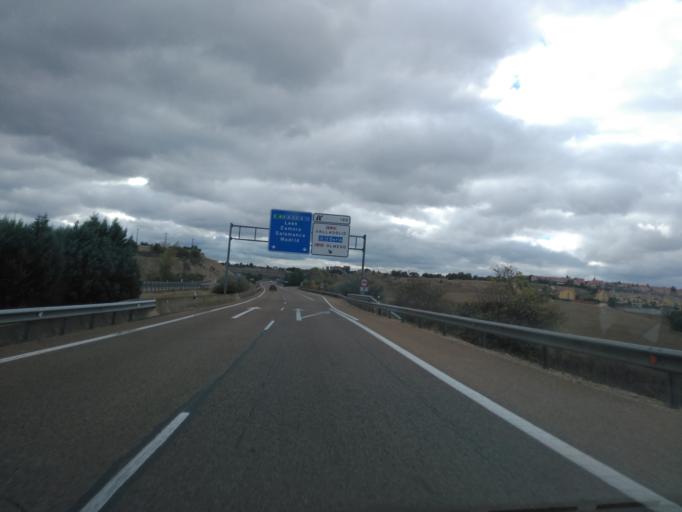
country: ES
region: Castille and Leon
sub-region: Provincia de Valladolid
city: Valladolid
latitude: 41.6896
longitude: -4.7267
